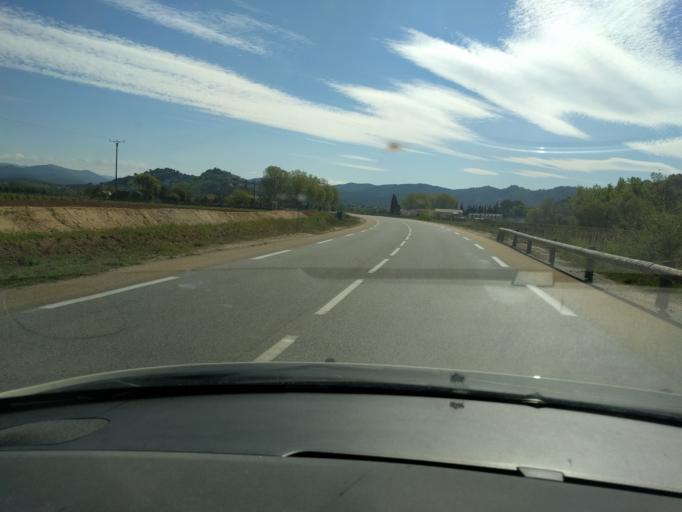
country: FR
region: Provence-Alpes-Cote d'Azur
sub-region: Departement du Var
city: Pierrefeu-du-Var
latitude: 43.2271
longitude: 6.1214
